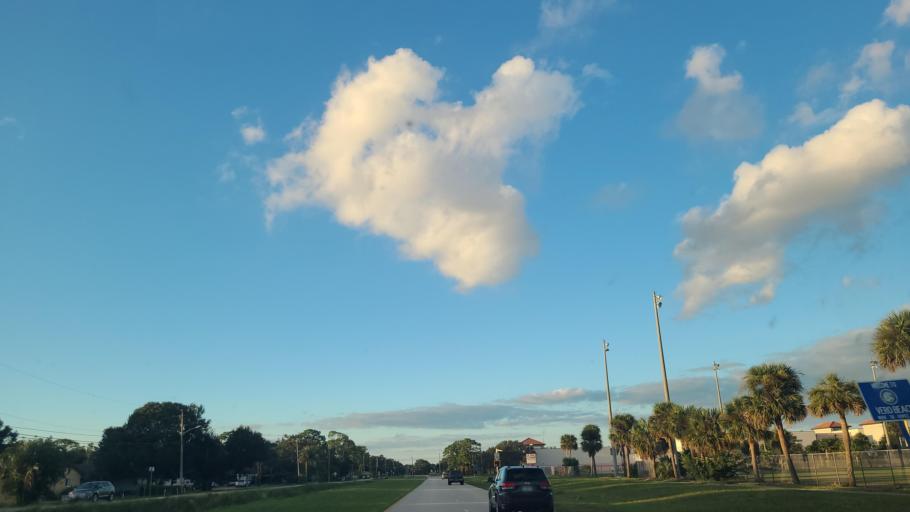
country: US
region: Florida
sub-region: Indian River County
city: Vero Beach South
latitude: 27.6271
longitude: -80.4057
